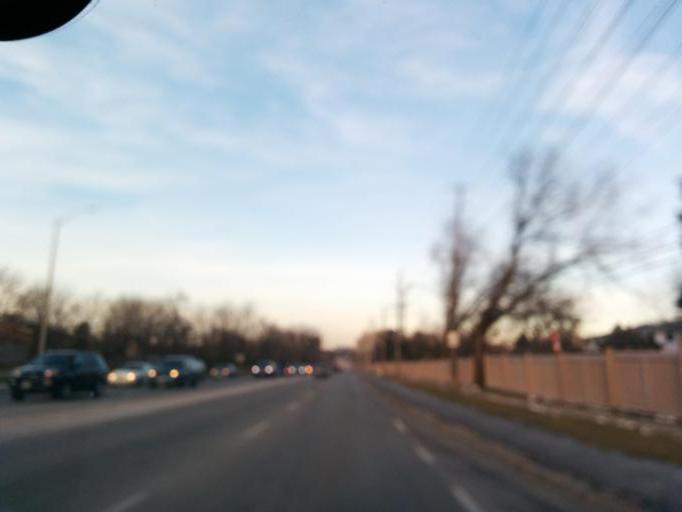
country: CA
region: Ontario
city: Etobicoke
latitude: 43.6288
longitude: -79.5956
